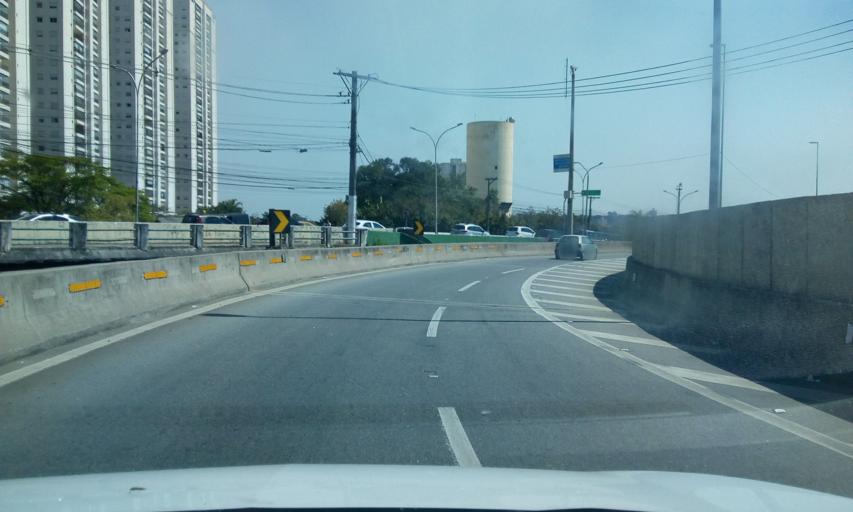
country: BR
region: Sao Paulo
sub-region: Osasco
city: Osasco
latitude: -23.5187
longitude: -46.7239
